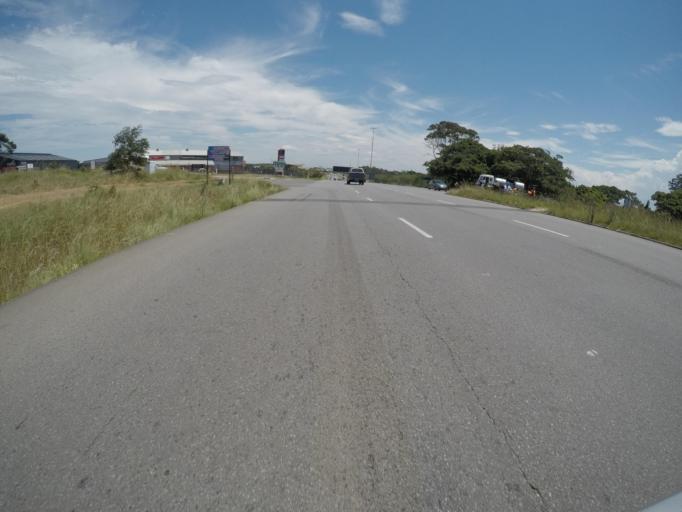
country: ZA
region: Eastern Cape
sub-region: Buffalo City Metropolitan Municipality
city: East London
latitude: -33.0353
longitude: 27.8413
